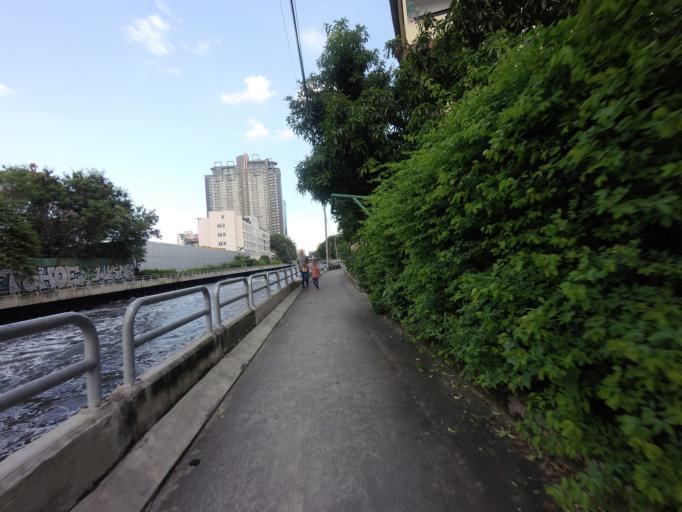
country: TH
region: Bangkok
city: Watthana
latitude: 13.7439
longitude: 100.5824
